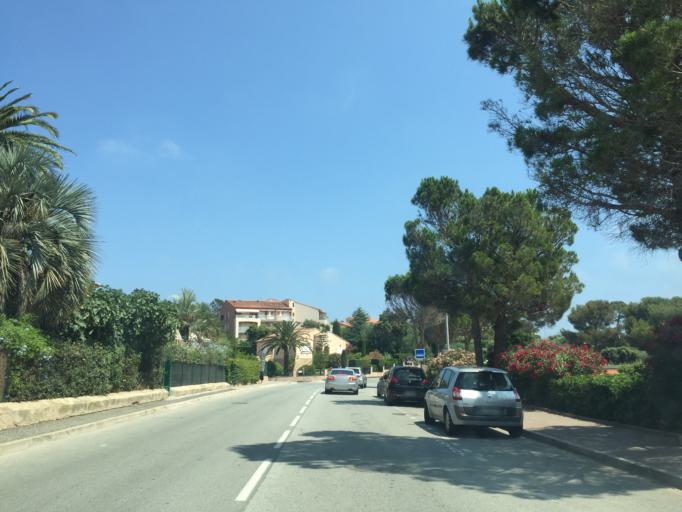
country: FR
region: Provence-Alpes-Cote d'Azur
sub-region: Departement du Var
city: Saint-Raphael
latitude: 43.4340
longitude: 6.8665
